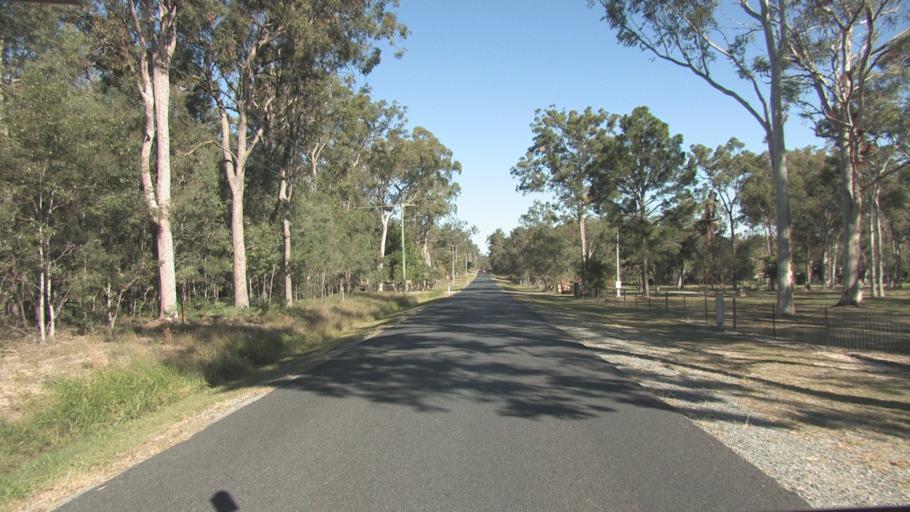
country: AU
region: Queensland
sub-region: Logan
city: Logan Reserve
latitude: -27.7270
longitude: 153.0729
